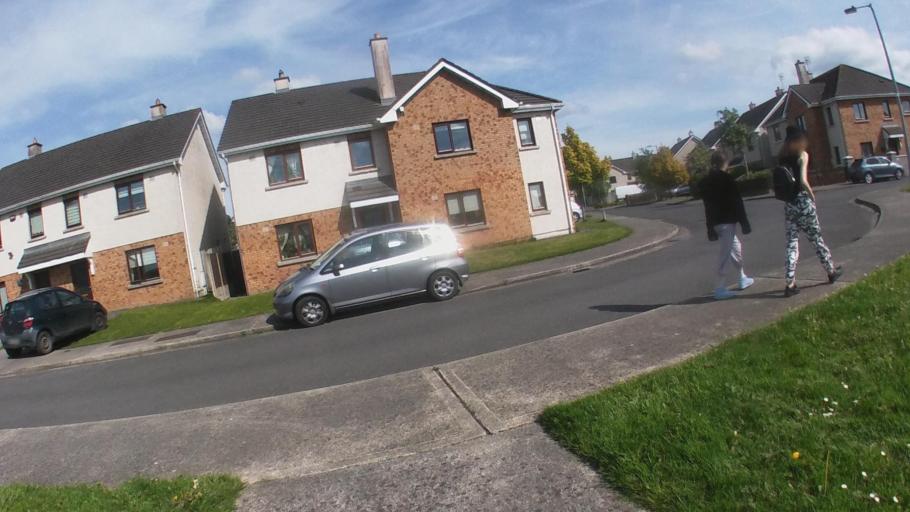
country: IE
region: Leinster
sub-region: County Carlow
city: Carlow
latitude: 52.8361
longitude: -6.9471
